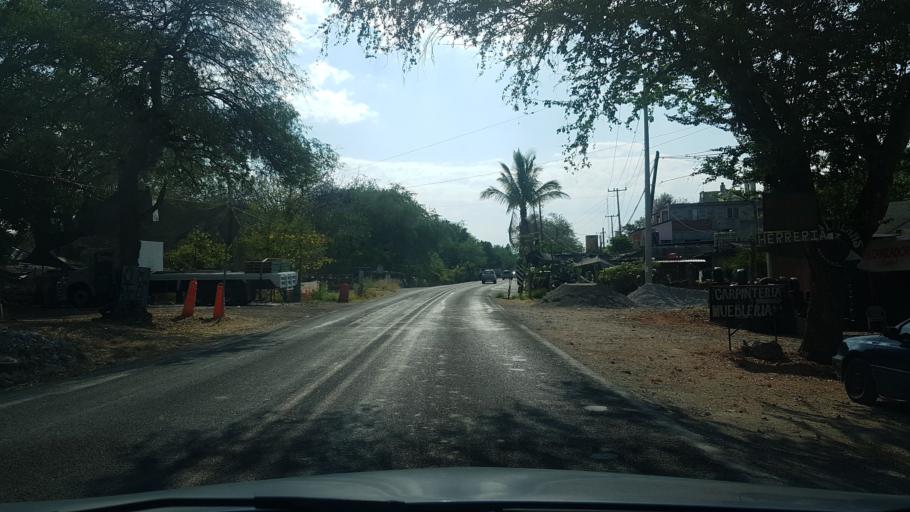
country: MX
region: Morelos
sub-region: Amacuzac
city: San Gabriel las Palmas
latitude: 18.6119
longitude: -99.3470
